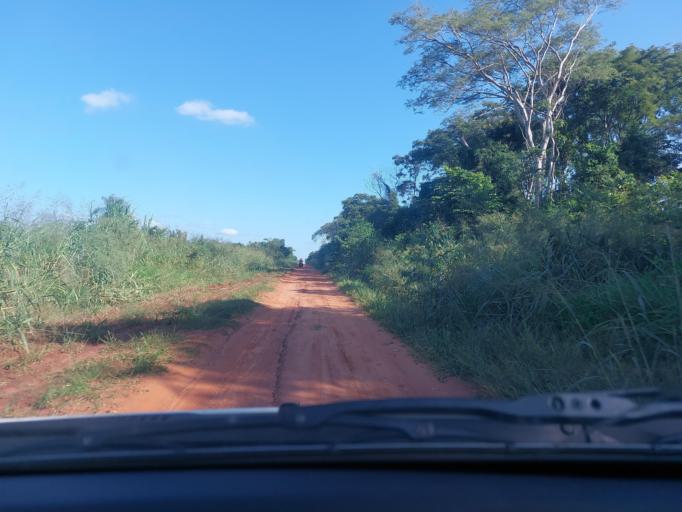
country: PY
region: San Pedro
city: Guayaybi
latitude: -24.5073
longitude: -56.5461
